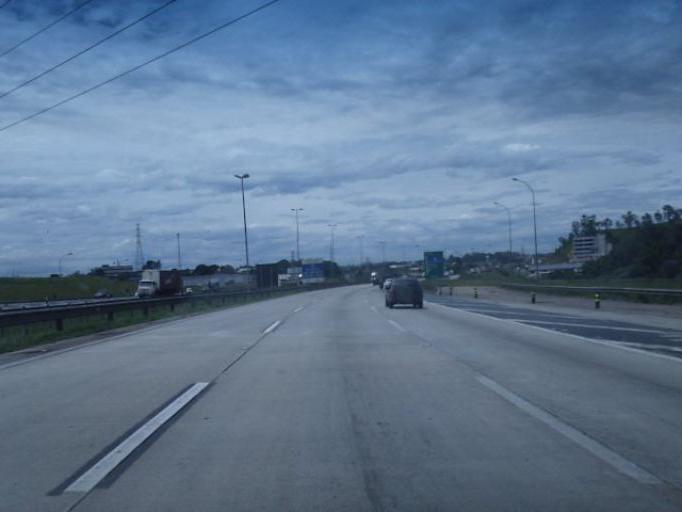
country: BR
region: Sao Paulo
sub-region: Embu
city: Embu
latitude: -23.6290
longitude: -46.8300
